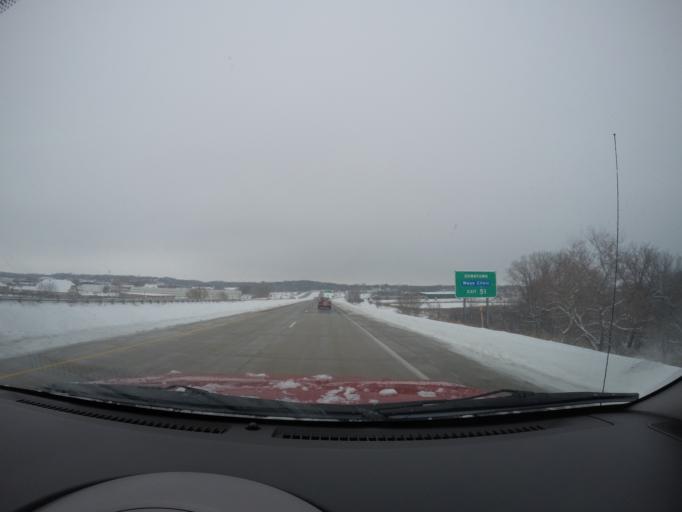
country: US
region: Minnesota
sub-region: Olmsted County
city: Rochester
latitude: 43.9747
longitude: -92.4534
